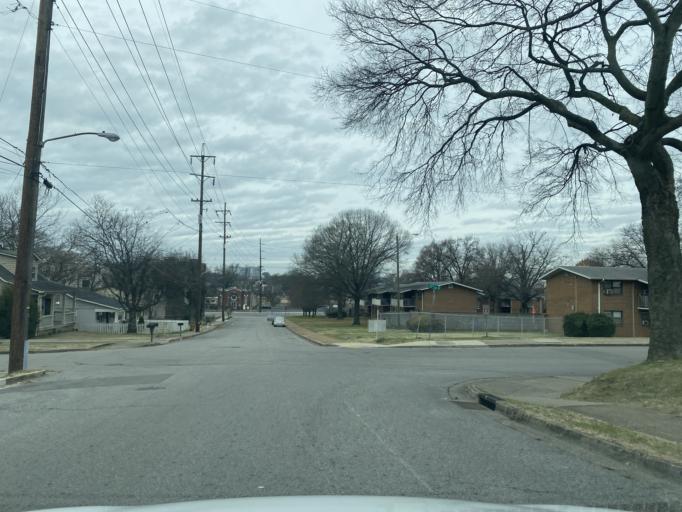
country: US
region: Tennessee
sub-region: Davidson County
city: Nashville
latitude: 36.1386
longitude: -86.7859
